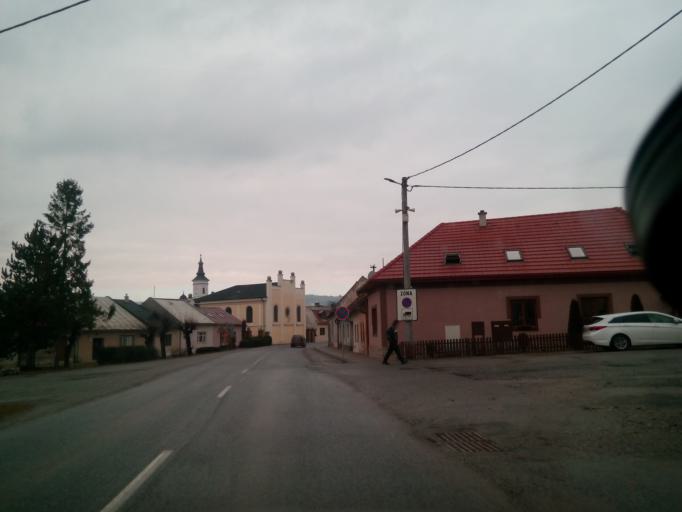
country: SK
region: Presovsky
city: Spisske Podhradie
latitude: 48.9971
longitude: 20.7551
